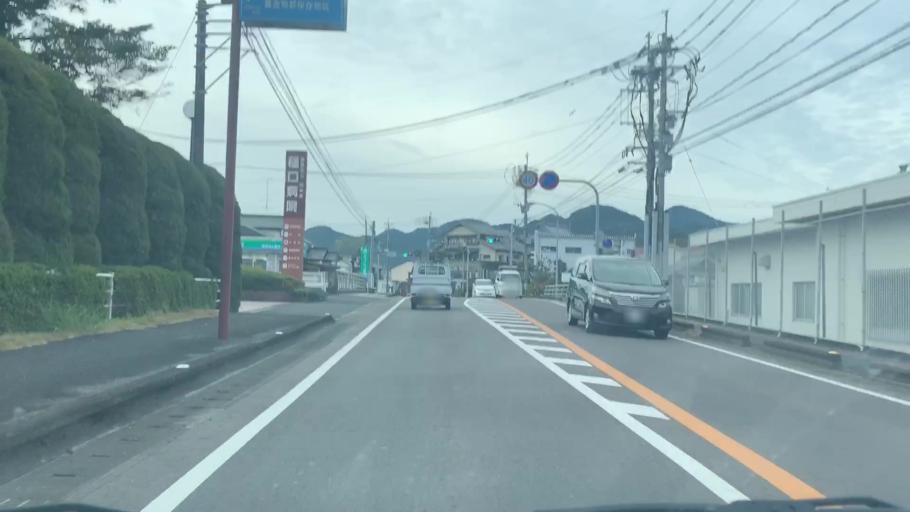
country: JP
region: Saga Prefecture
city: Kashima
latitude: 33.1331
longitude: 130.0617
